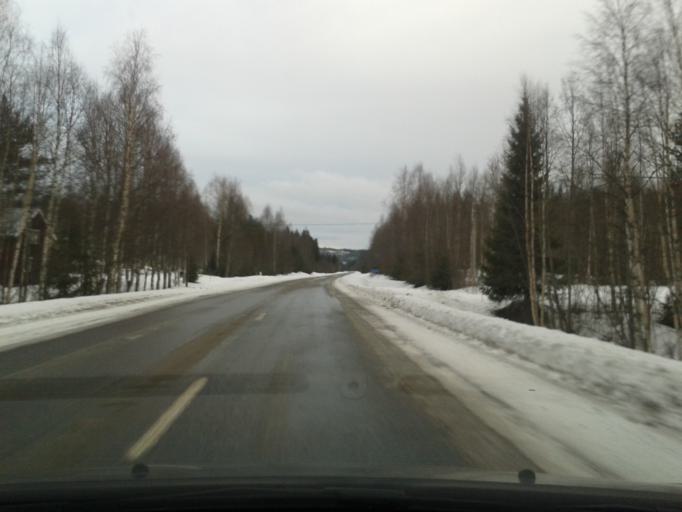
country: SE
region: Vaesternorrland
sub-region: Solleftea Kommun
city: As
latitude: 63.6315
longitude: 16.8140
